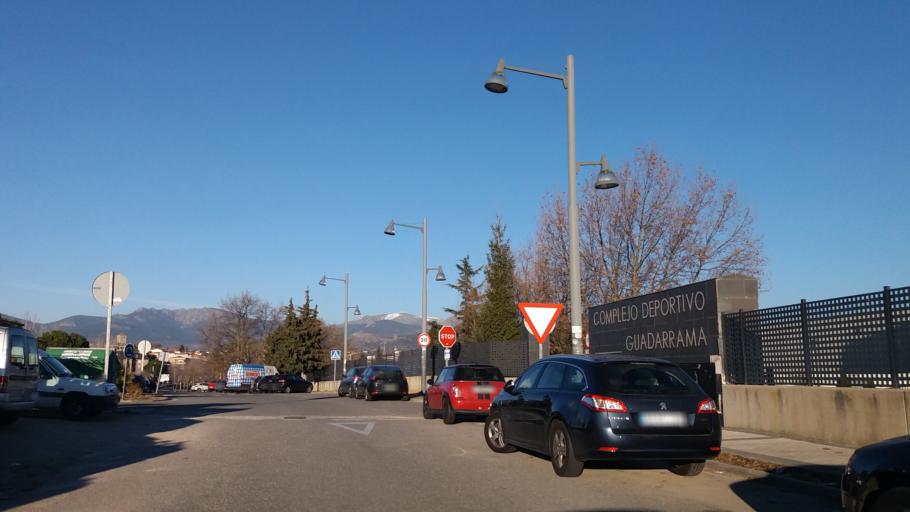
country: ES
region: Madrid
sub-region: Provincia de Madrid
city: Guadarrama
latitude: 40.6643
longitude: -4.0899
